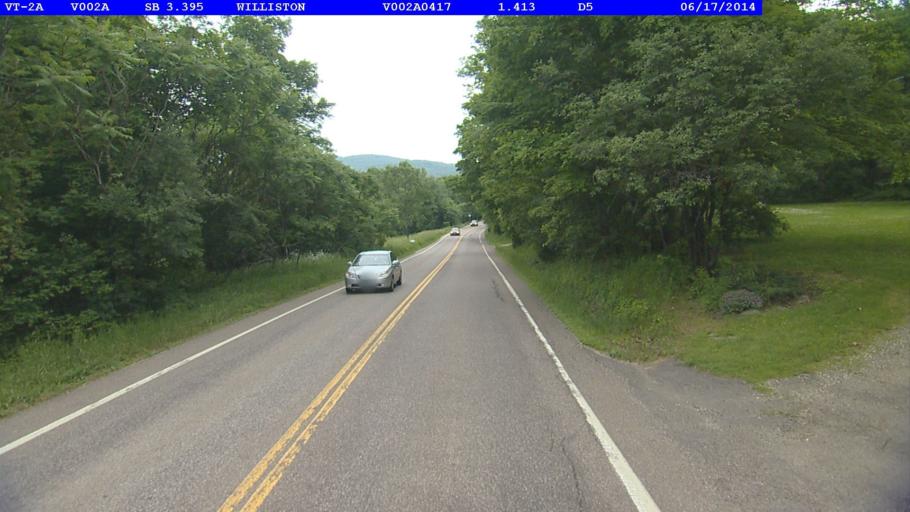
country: US
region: Vermont
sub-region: Chittenden County
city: Williston
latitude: 44.4180
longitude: -73.1240
